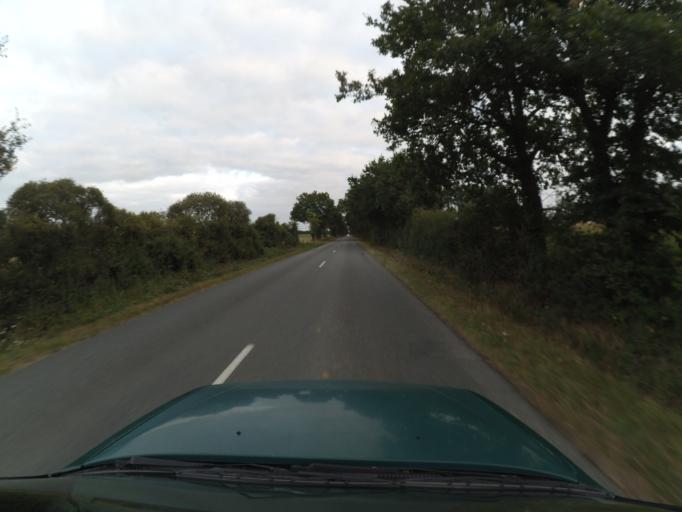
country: FR
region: Pays de la Loire
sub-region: Departement de la Loire-Atlantique
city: Montbert
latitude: 47.0106
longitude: -1.4783
